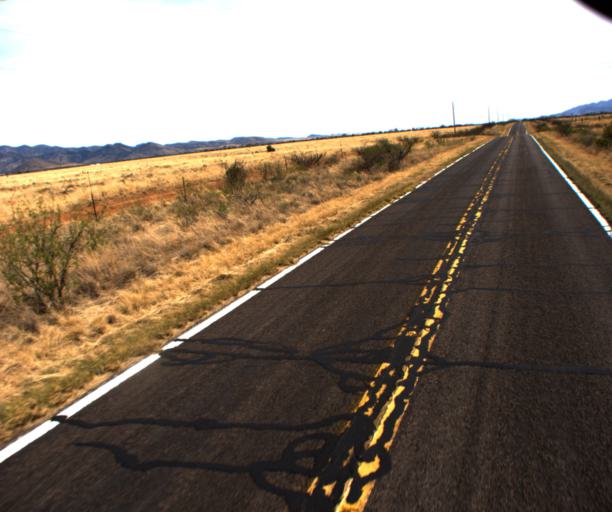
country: US
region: Arizona
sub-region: Cochise County
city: Willcox
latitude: 31.9078
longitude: -109.4914
